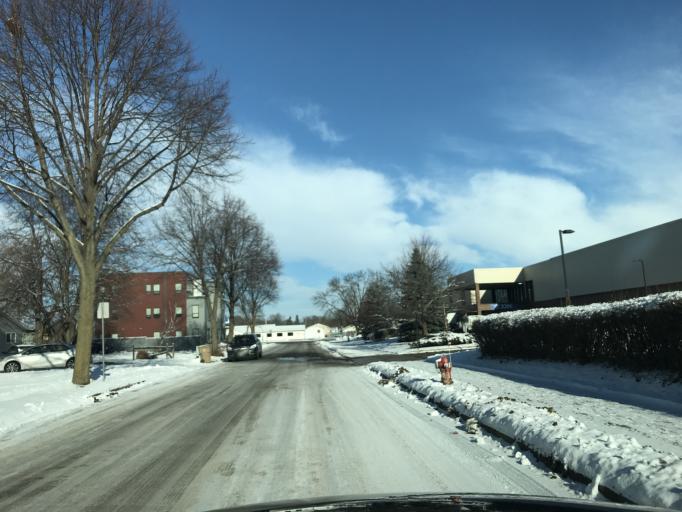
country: US
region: Wisconsin
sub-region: Dane County
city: Monona
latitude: 43.0825
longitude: -89.3150
